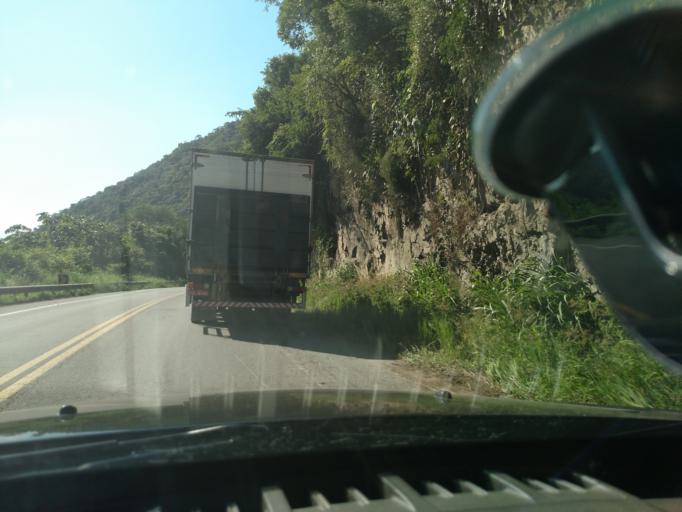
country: BR
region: Santa Catarina
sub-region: Ibirama
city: Ibirama
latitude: -27.0906
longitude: -49.4706
